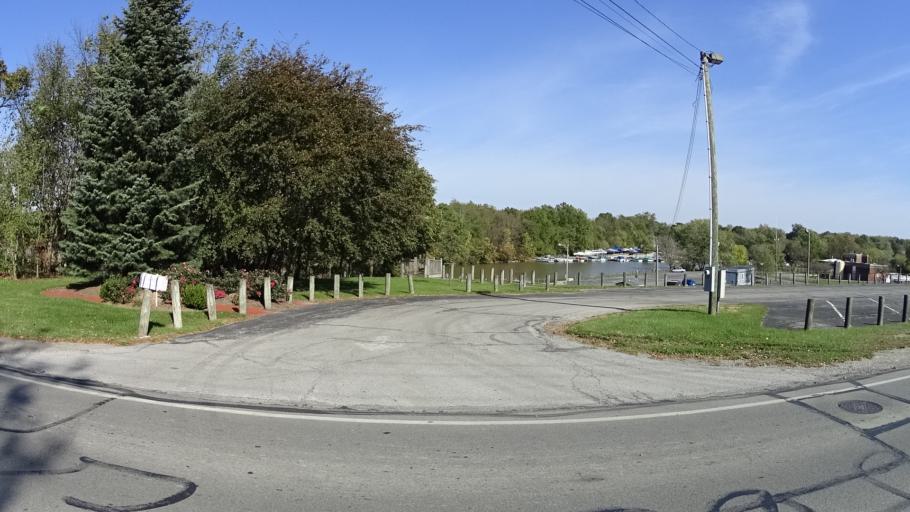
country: US
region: Ohio
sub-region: Lorain County
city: Vermilion
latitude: 41.4199
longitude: -82.3577
